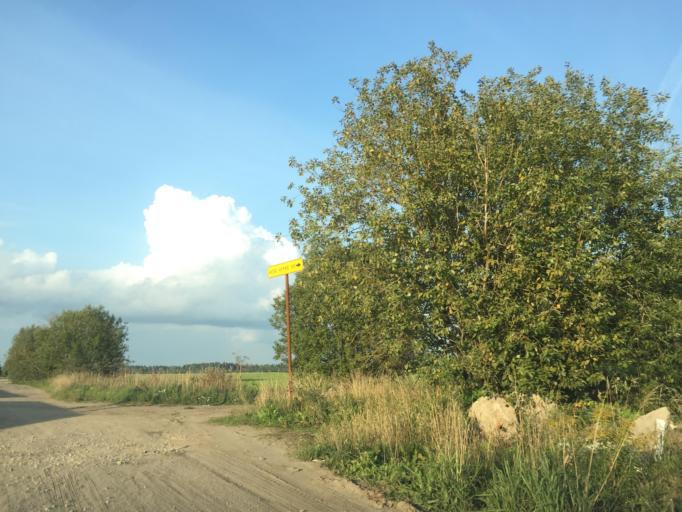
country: RU
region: Leningrad
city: Rozhdestveno
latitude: 59.3499
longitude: 29.9659
